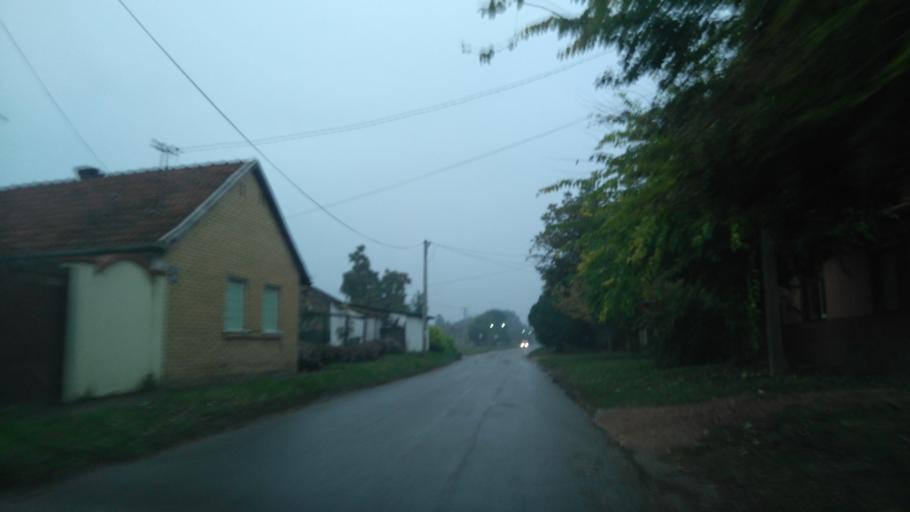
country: RS
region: Autonomna Pokrajina Vojvodina
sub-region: Juznobacki Okrug
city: Becej
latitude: 45.6253
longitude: 20.0445
